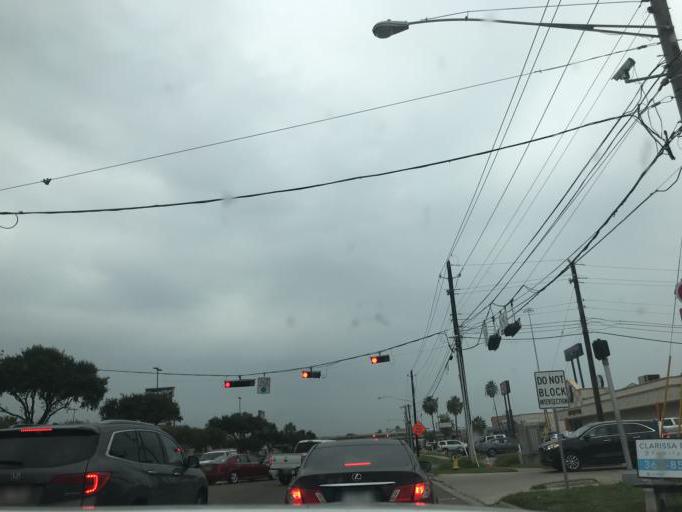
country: US
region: Texas
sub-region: Nueces County
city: Corpus Christi
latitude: 27.7057
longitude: -97.3712
